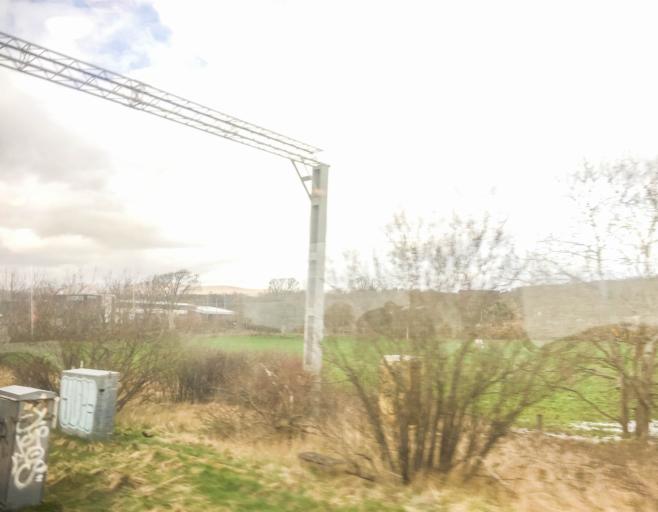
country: GB
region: Scotland
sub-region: Argyll and Bute
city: Helensburgh
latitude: 55.9920
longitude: -4.7005
